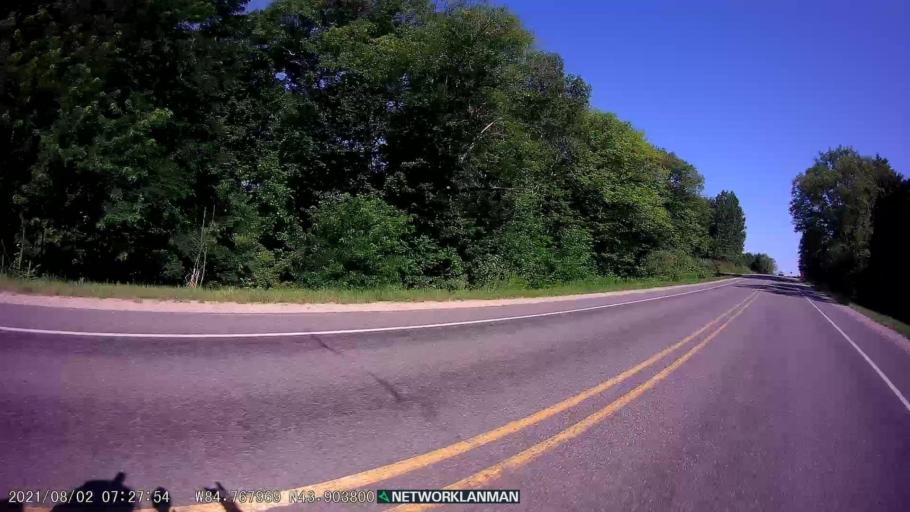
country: US
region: Michigan
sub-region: Clare County
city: Clare
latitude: 43.9035
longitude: -84.7679
